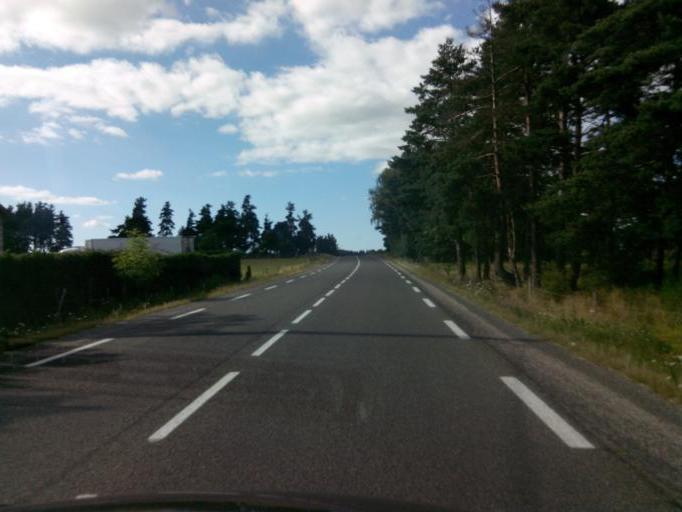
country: FR
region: Auvergne
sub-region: Departement de la Haute-Loire
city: Saint-Paulien
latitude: 45.1986
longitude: 3.8206
